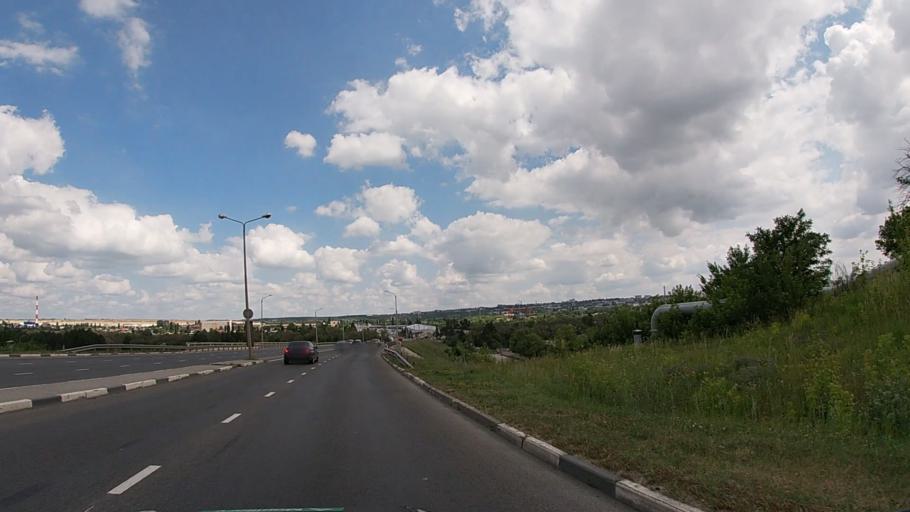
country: RU
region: Belgorod
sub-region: Belgorodskiy Rayon
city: Belgorod
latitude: 50.6052
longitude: 36.5304
